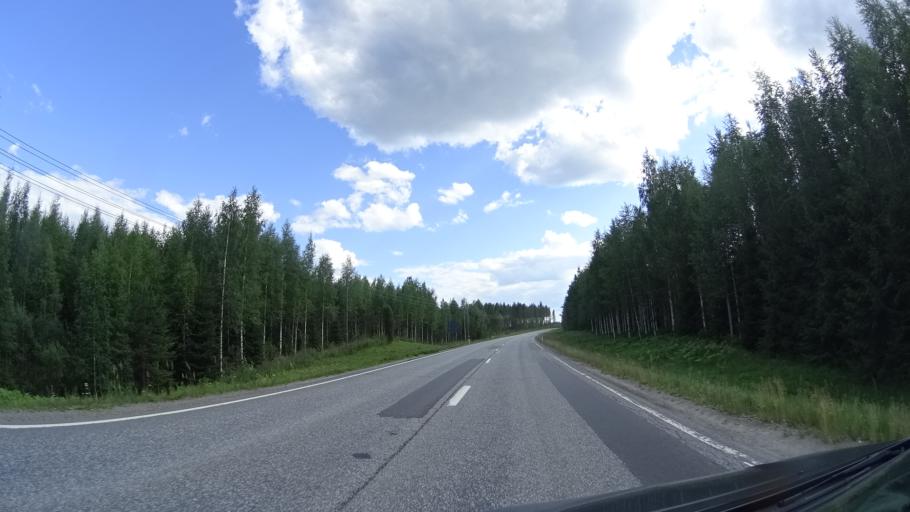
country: FI
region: Southern Savonia
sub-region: Savonlinna
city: Punkaharju
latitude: 61.6755
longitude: 29.4136
